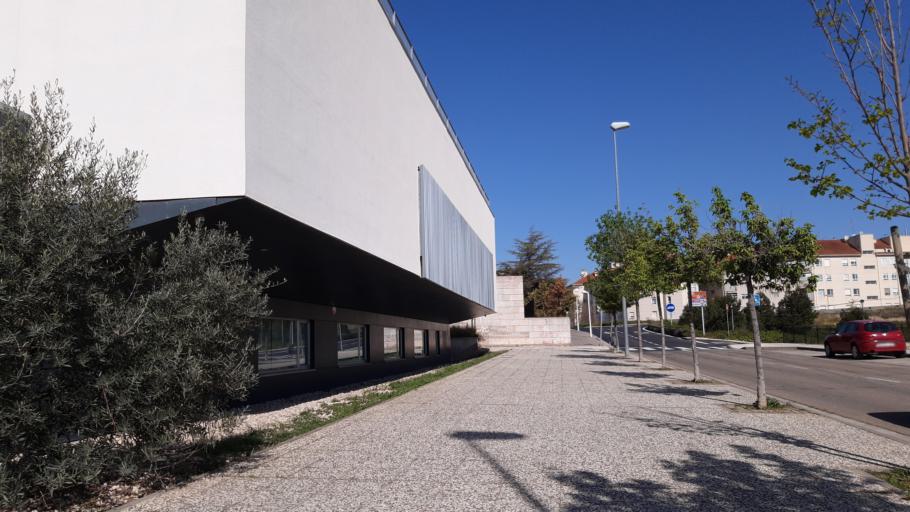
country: ES
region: Aragon
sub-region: Provincia de Zaragoza
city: Utebo
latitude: 41.7078
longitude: -0.9958
